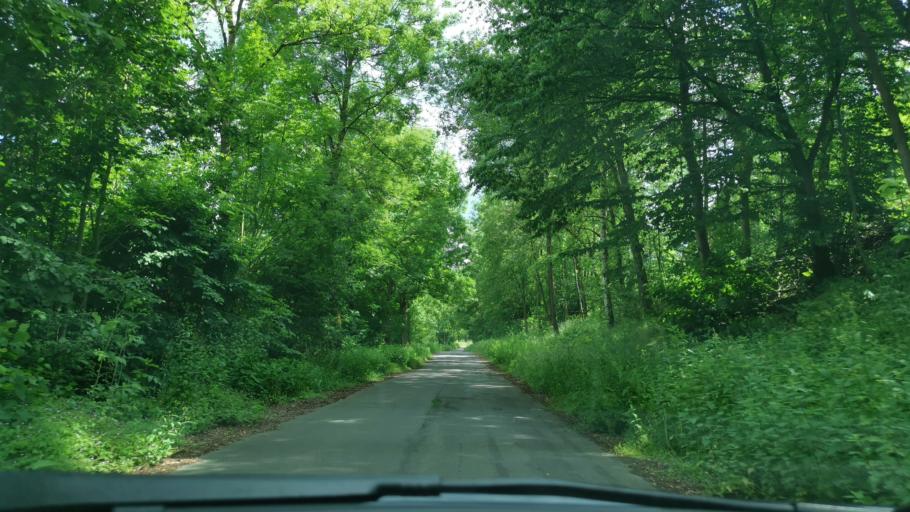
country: DE
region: Hesse
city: Waldkappel
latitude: 51.1720
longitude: 9.8252
